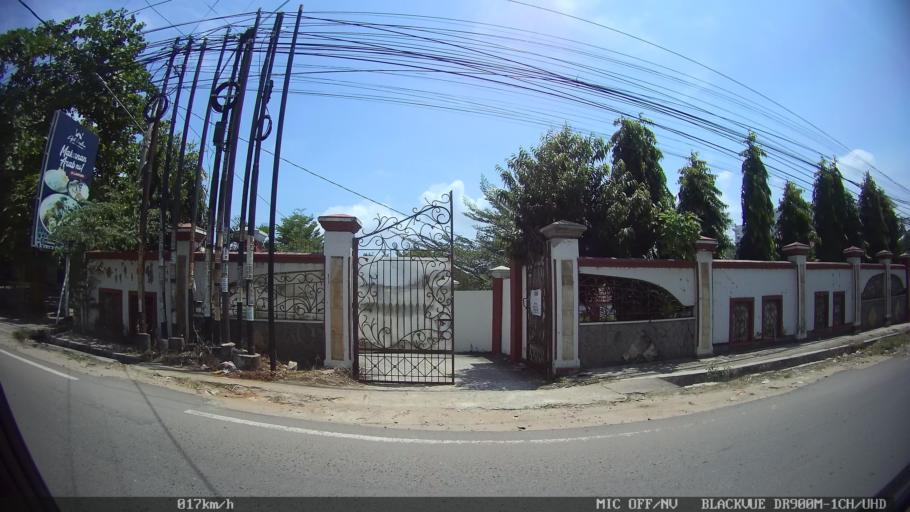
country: ID
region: Lampung
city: Kedaton
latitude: -5.3919
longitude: 105.2779
